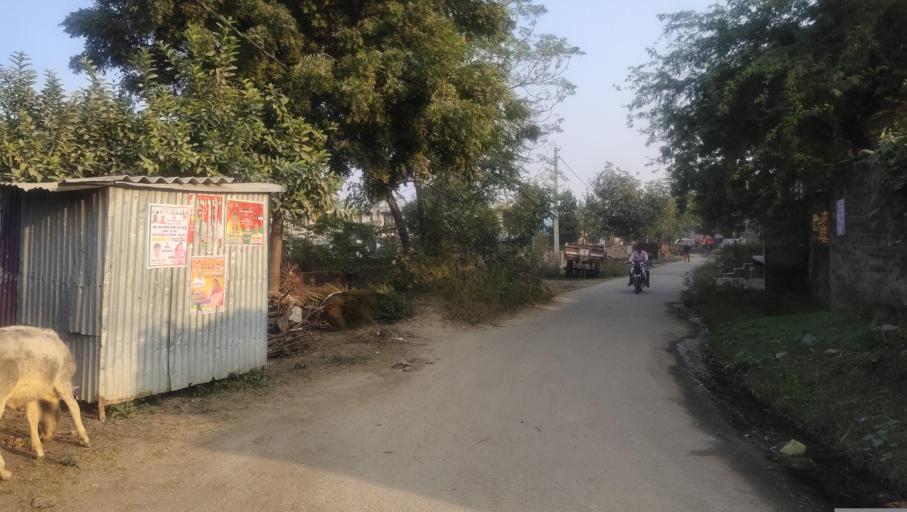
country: IN
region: Uttar Pradesh
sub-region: Lucknow District
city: Goshainganj
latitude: 26.7914
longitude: 81.0123
